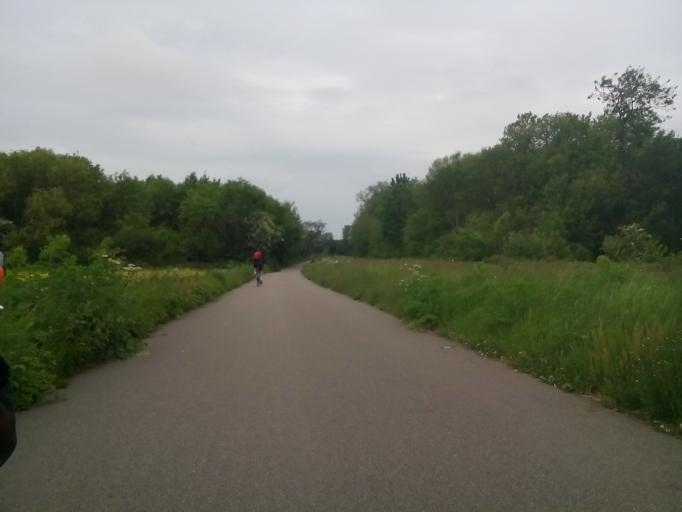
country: GB
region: England
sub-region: Cambridgeshire
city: Histon
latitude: 52.2617
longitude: 0.0803
